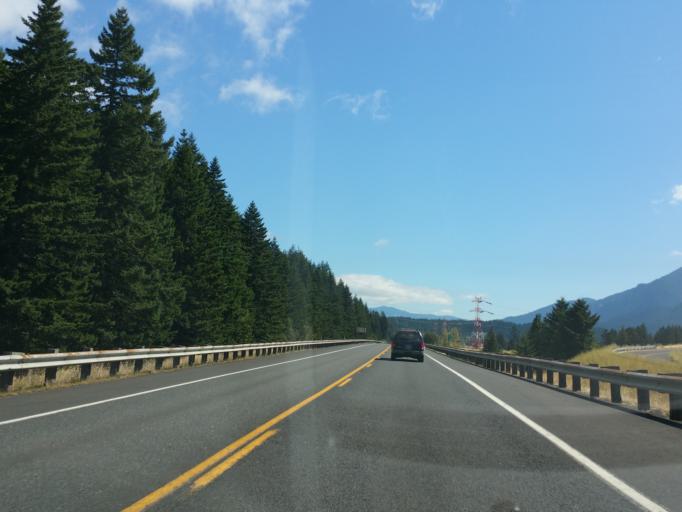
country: US
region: Oregon
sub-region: Hood River County
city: Cascade Locks
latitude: 45.6420
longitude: -121.9673
